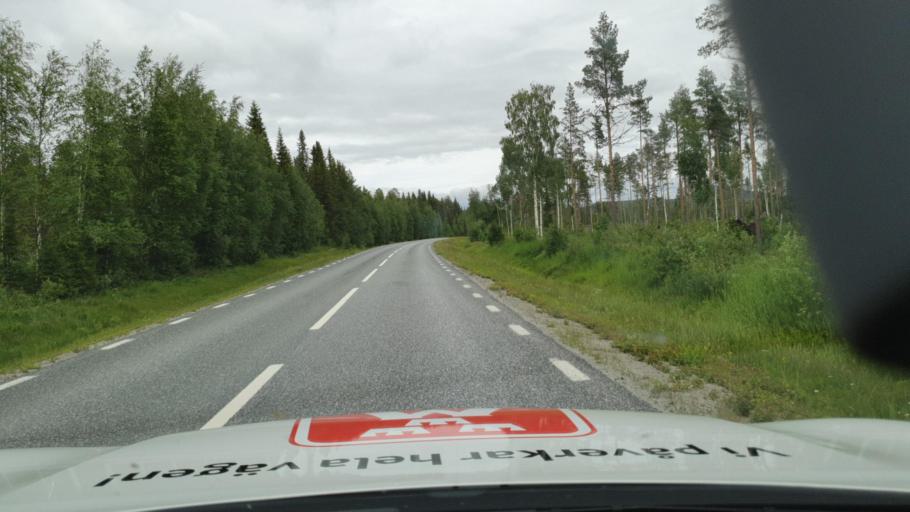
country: SE
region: Vaesterbotten
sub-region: Asele Kommun
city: Insjon
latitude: 64.3329
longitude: 17.7426
